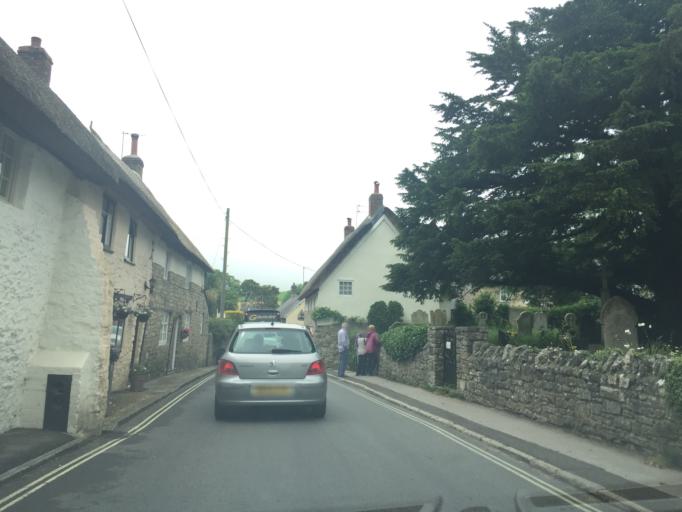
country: GB
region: England
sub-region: Dorset
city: Wool
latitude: 50.6261
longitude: -2.2466
